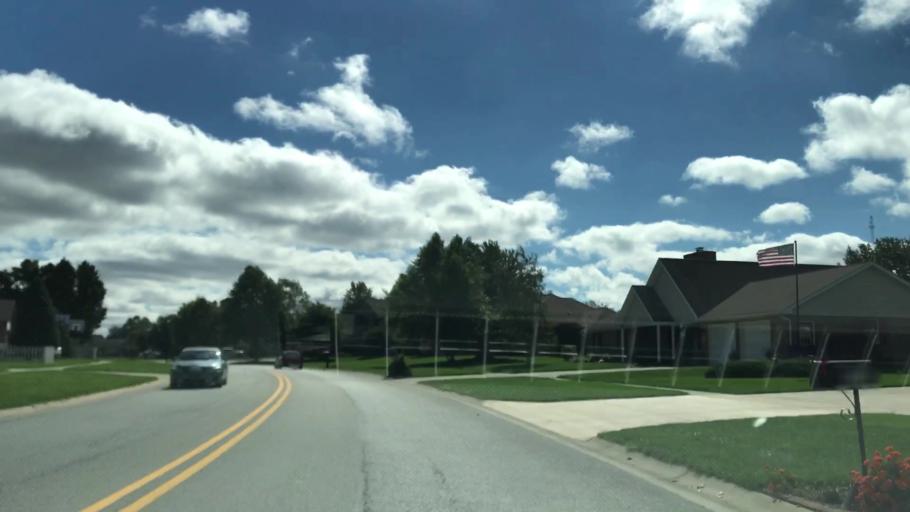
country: US
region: Indiana
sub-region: Howard County
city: Indian Heights
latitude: 40.4388
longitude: -86.1081
